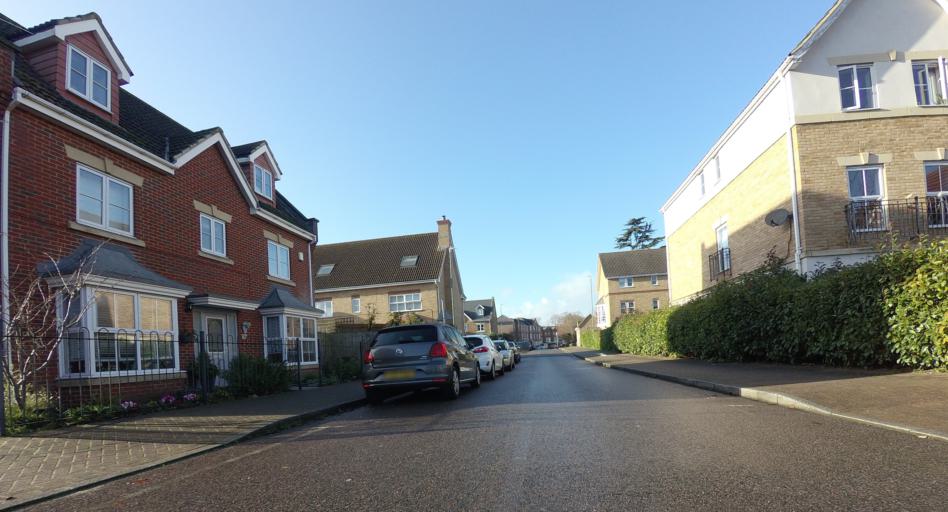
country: GB
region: England
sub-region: Greater London
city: Bexley
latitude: 51.4327
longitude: 0.1767
